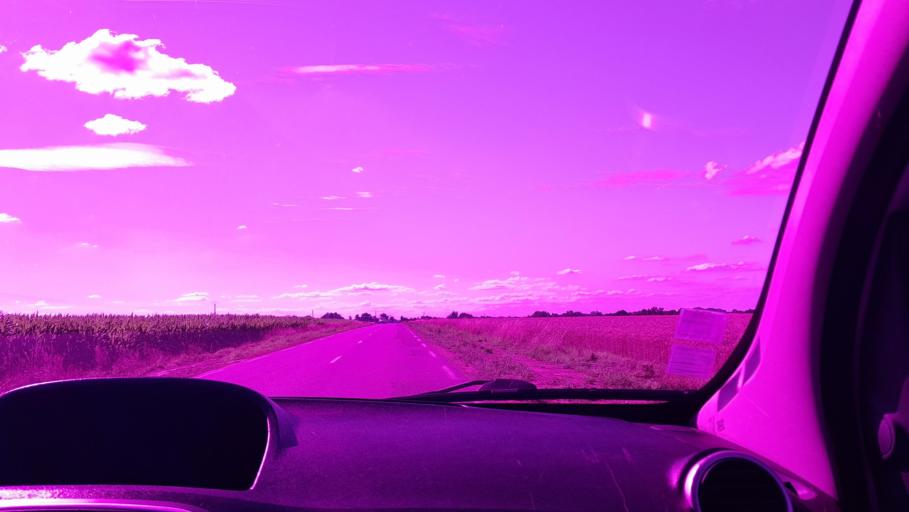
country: FR
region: Pays de la Loire
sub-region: Departement de la Mayenne
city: Craon
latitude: 47.8627
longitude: -0.9843
